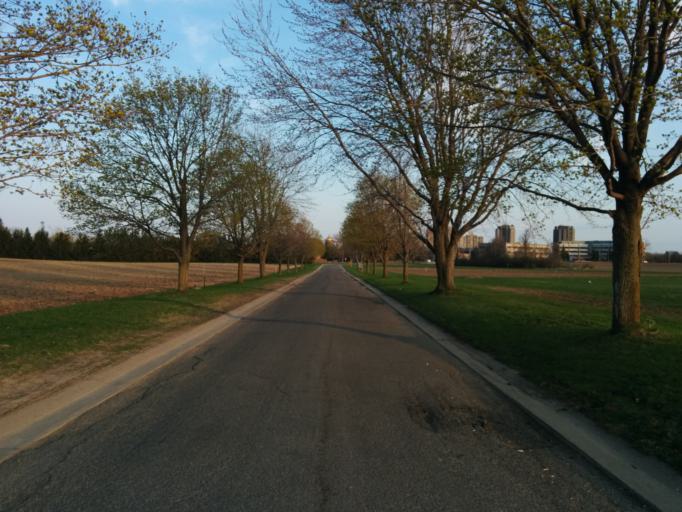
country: CA
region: Ontario
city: Ottawa
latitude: 45.3812
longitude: -75.7072
